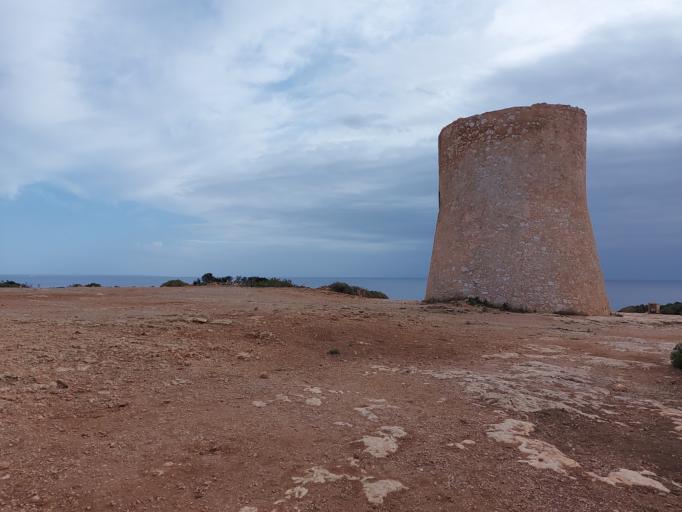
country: ES
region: Balearic Islands
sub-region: Illes Balears
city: Llucmajor
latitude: 39.3618
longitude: 2.8352
